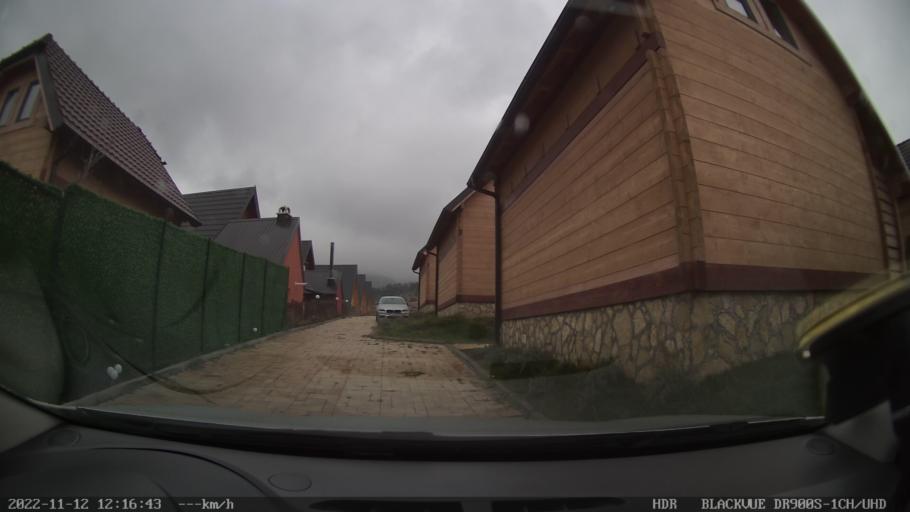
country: RS
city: Zlatibor
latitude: 43.7030
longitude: 19.7255
